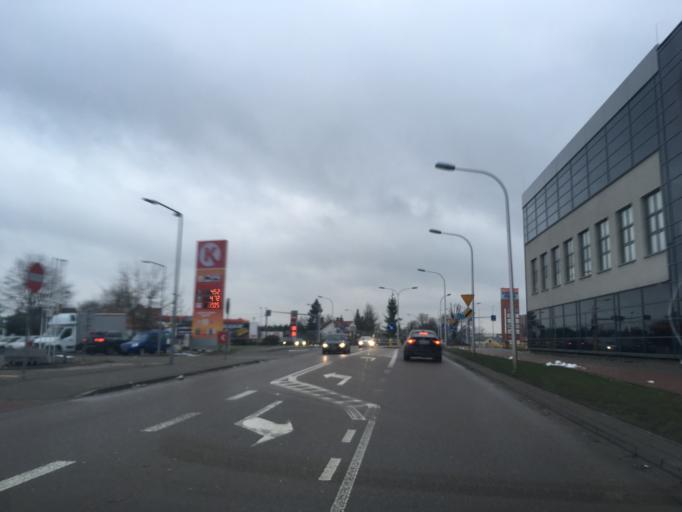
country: PL
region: Podlasie
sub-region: Suwalki
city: Suwalki
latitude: 54.1101
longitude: 22.9279
